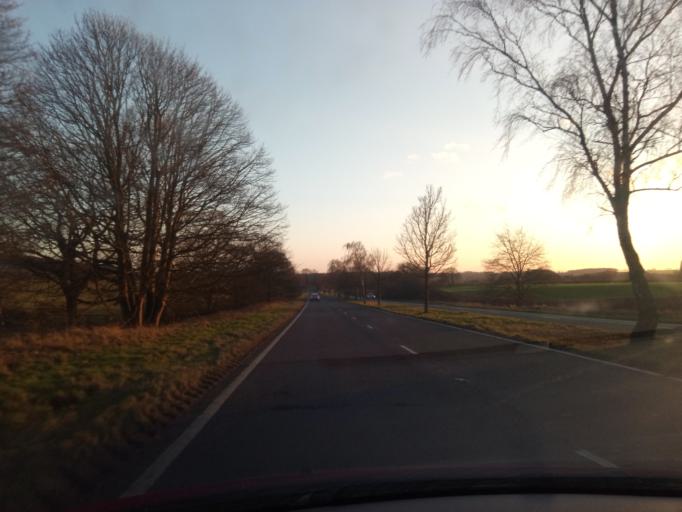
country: GB
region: England
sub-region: Nottinghamshire
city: Farnsfield
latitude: 53.0576
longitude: -1.0696
